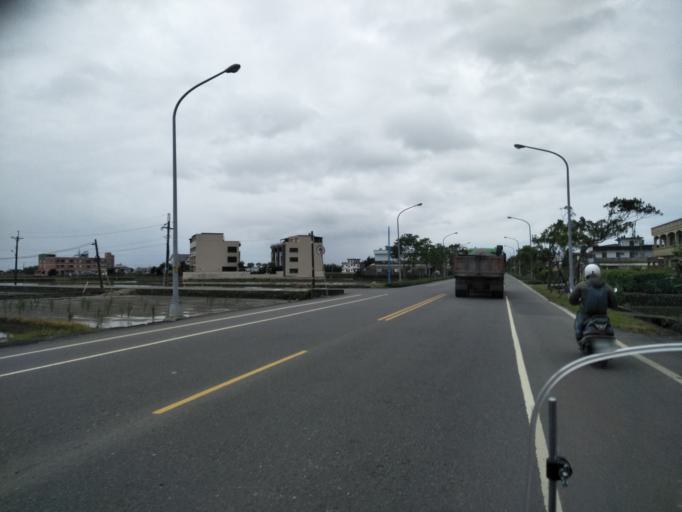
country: TW
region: Taiwan
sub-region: Yilan
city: Yilan
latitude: 24.7910
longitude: 121.7844
